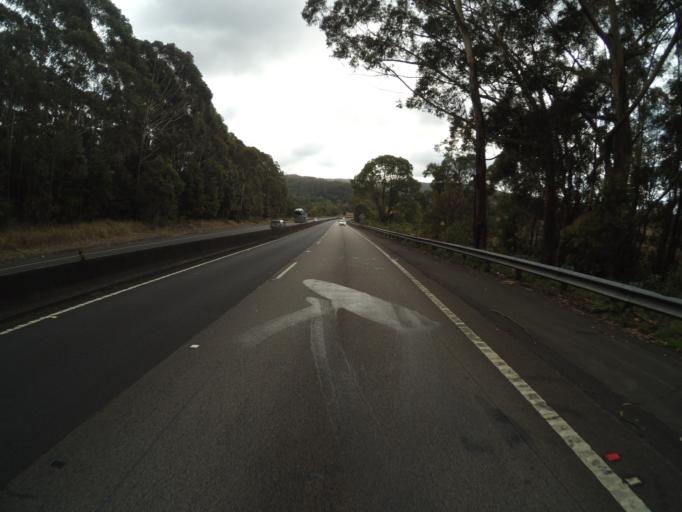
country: AU
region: New South Wales
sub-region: Wollongong
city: Bulli
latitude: -34.3438
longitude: 150.8770
